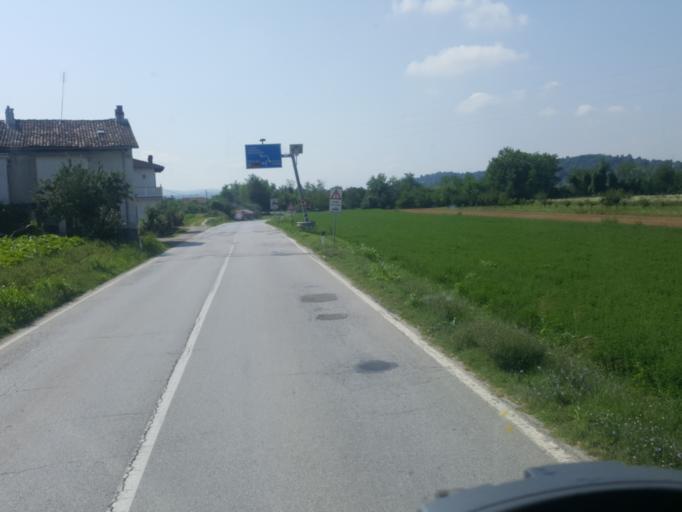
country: IT
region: Piedmont
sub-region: Provincia di Cuneo
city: Narzole
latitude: 44.6002
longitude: 7.8917
